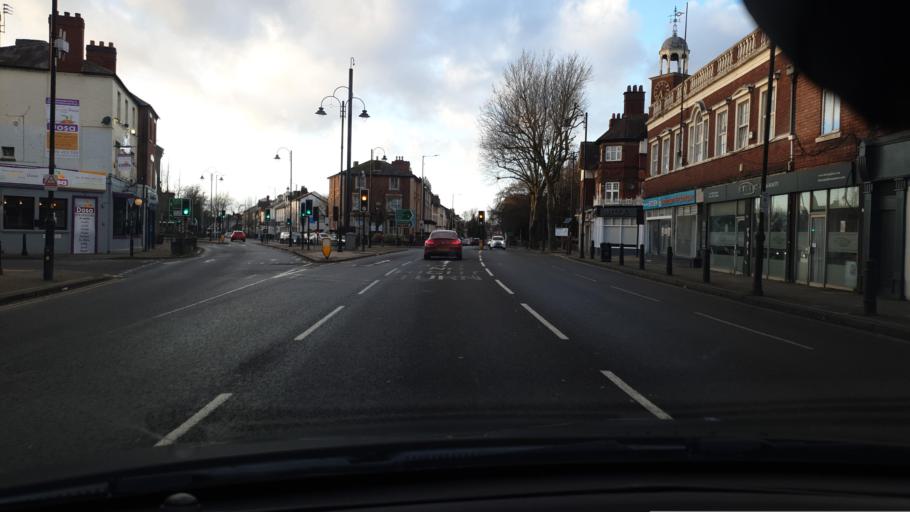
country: GB
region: England
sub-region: Wolverhampton
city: Wolverhampton
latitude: 52.5853
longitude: -2.1392
